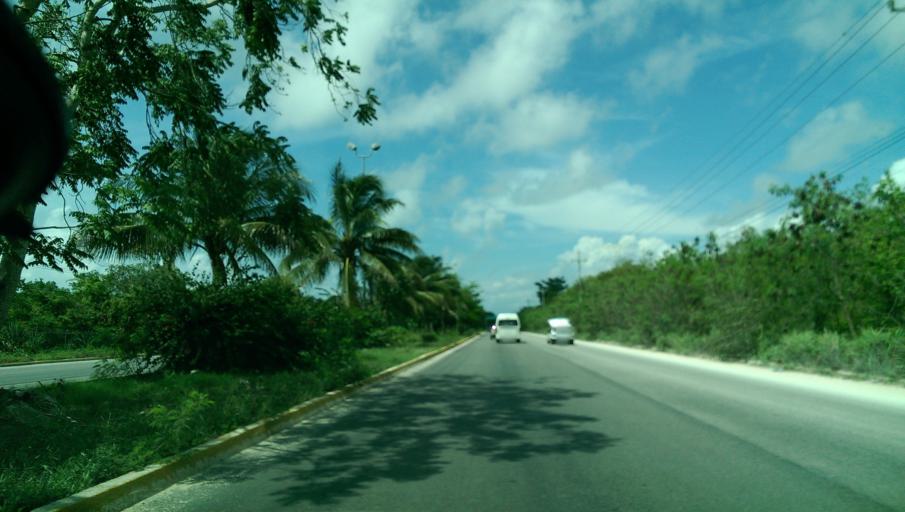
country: MX
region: Quintana Roo
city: Playa del Carmen
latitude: 20.7107
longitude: -87.0200
